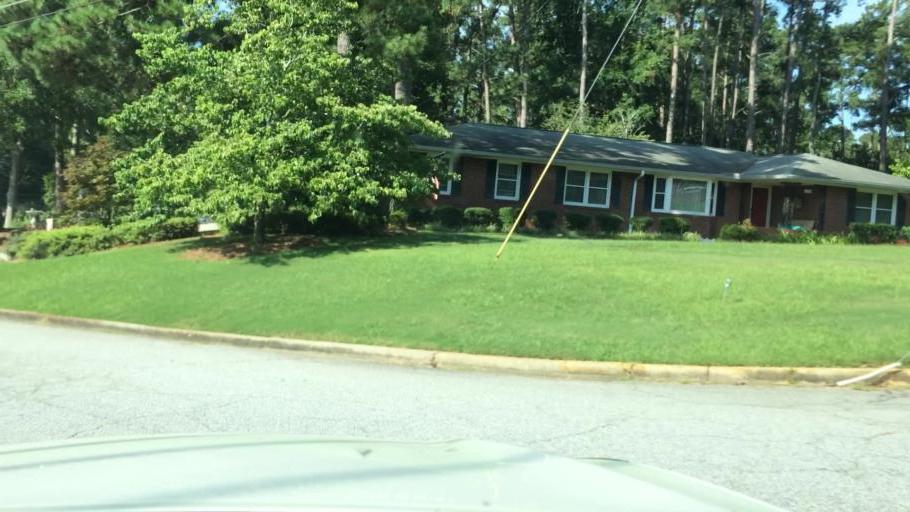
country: US
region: Georgia
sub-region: Columbia County
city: Martinez
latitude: 33.4941
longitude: -82.0384
